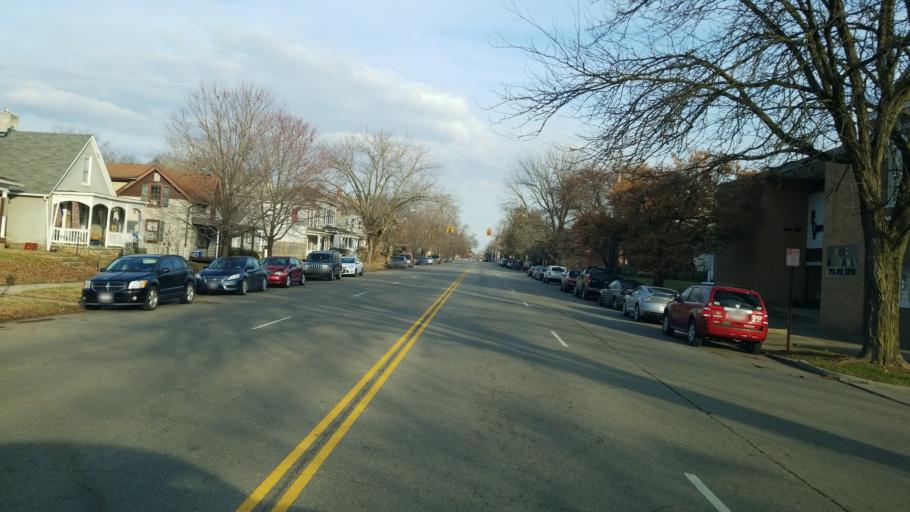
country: US
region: Ohio
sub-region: Ross County
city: Chillicothe
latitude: 39.3273
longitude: -82.9806
